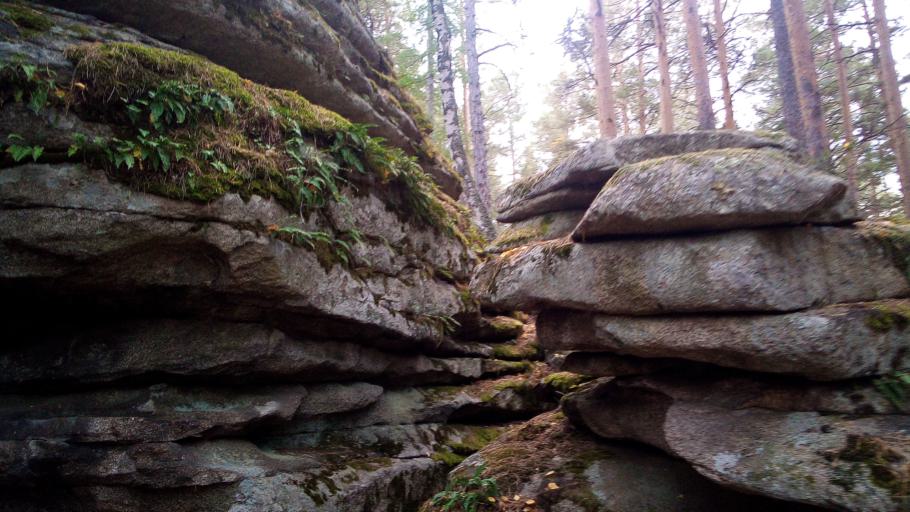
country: RU
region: Chelyabinsk
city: Turgoyak
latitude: 55.1752
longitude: 60.0208
